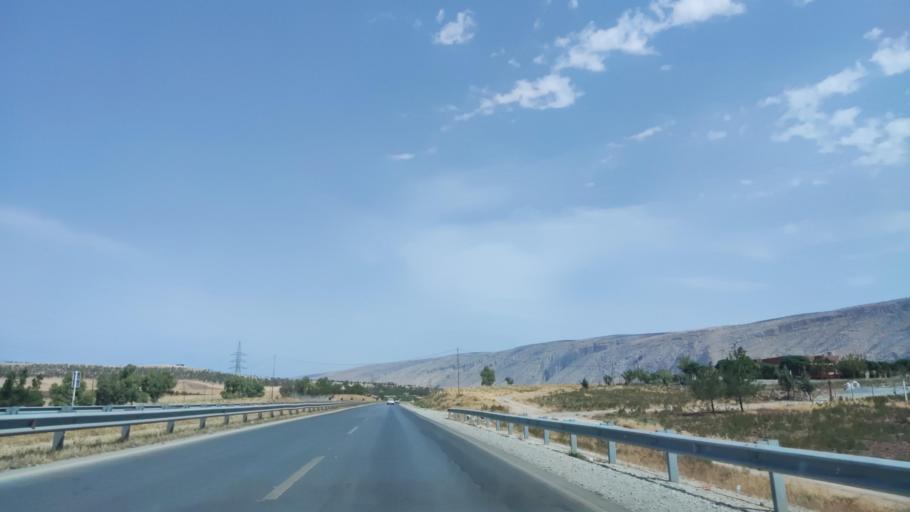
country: IQ
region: Arbil
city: Shaqlawah
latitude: 36.4741
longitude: 44.3812
